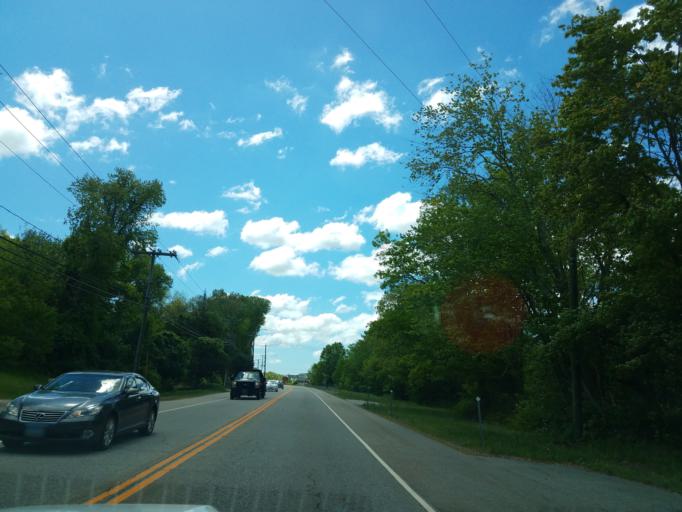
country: US
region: Connecticut
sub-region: New London County
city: Montville Center
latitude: 41.4360
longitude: -72.2250
